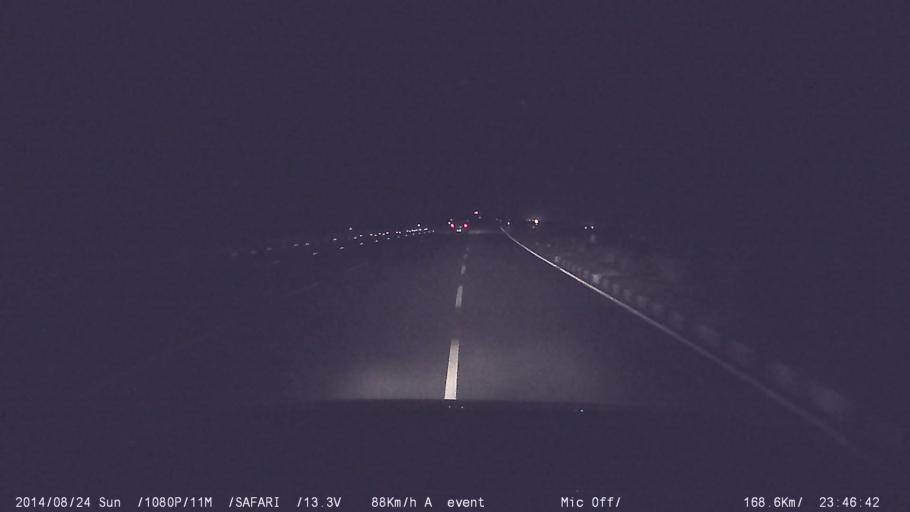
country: IN
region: Tamil Nadu
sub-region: Krishnagiri
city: Krishnagiri
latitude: 12.5519
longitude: 78.3472
